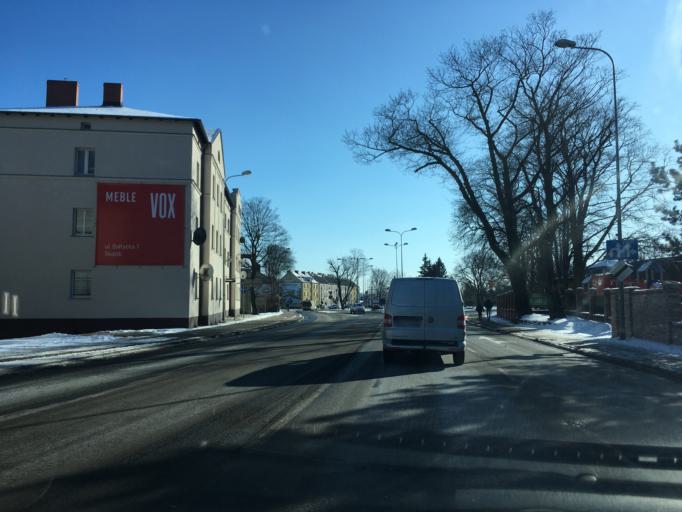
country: PL
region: Pomeranian Voivodeship
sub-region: Slupsk
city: Slupsk
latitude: 54.4648
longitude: 17.0112
